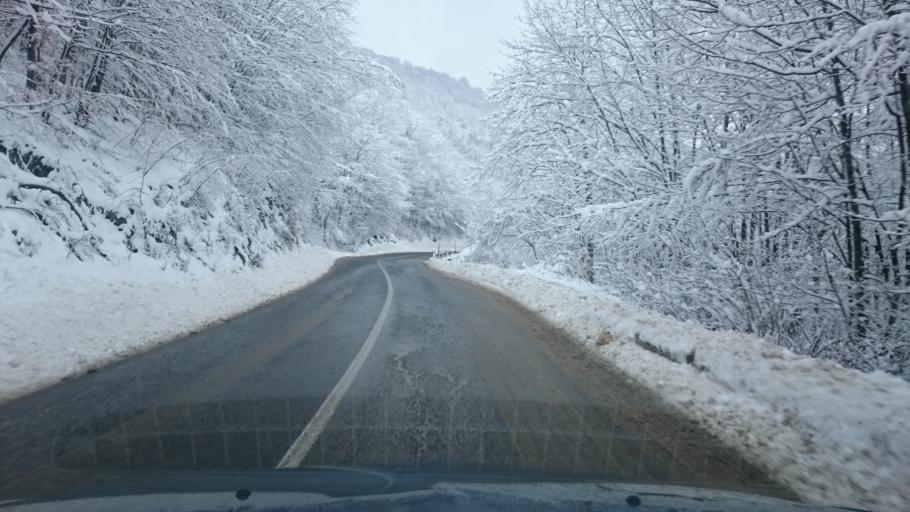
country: BA
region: Republika Srpska
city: Kotor-Varos
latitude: 44.5876
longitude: 17.2294
